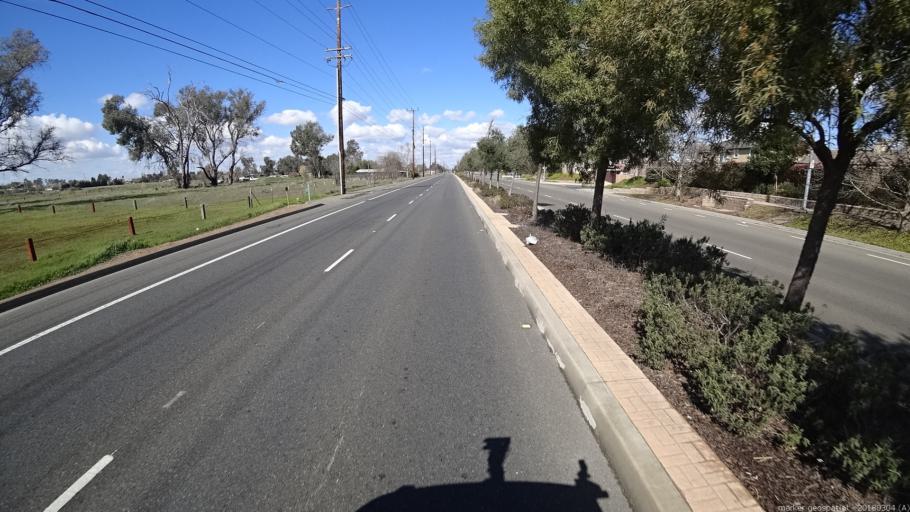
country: US
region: California
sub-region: Sacramento County
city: Vineyard
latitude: 38.4663
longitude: -121.3348
